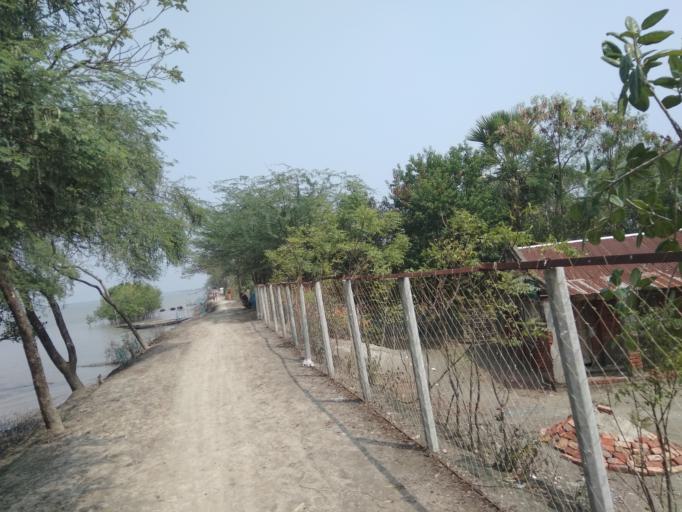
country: IN
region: West Bengal
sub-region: North 24 Parganas
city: Gosaba
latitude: 22.2482
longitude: 89.2499
